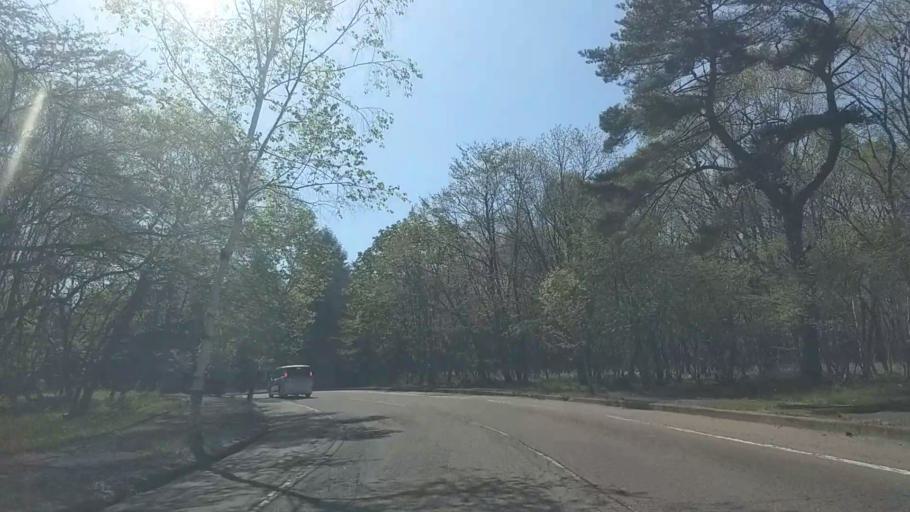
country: JP
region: Yamanashi
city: Nirasaki
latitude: 35.9415
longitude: 138.4366
